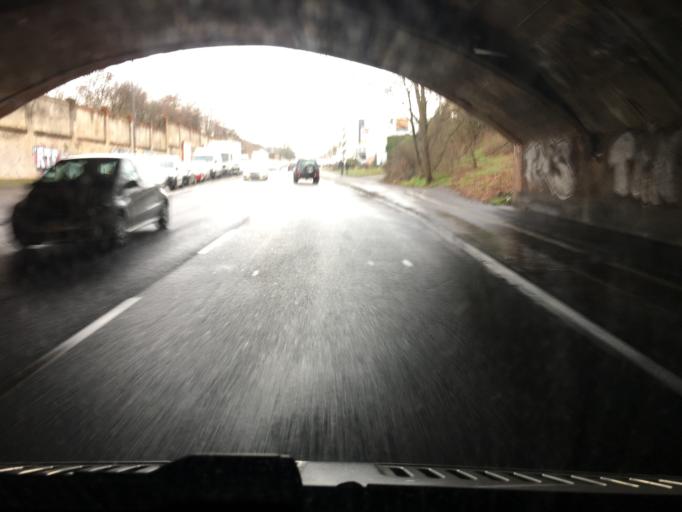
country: DE
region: North Rhine-Westphalia
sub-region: Regierungsbezirk Koln
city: Bilderstoeckchen
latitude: 50.9496
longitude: 6.8976
